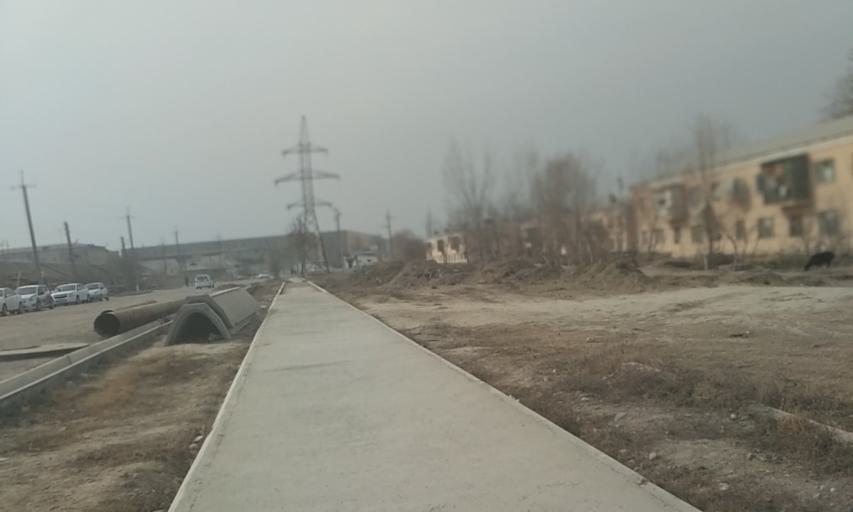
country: UZ
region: Sirdaryo
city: Guliston
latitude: 40.5057
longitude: 68.7775
